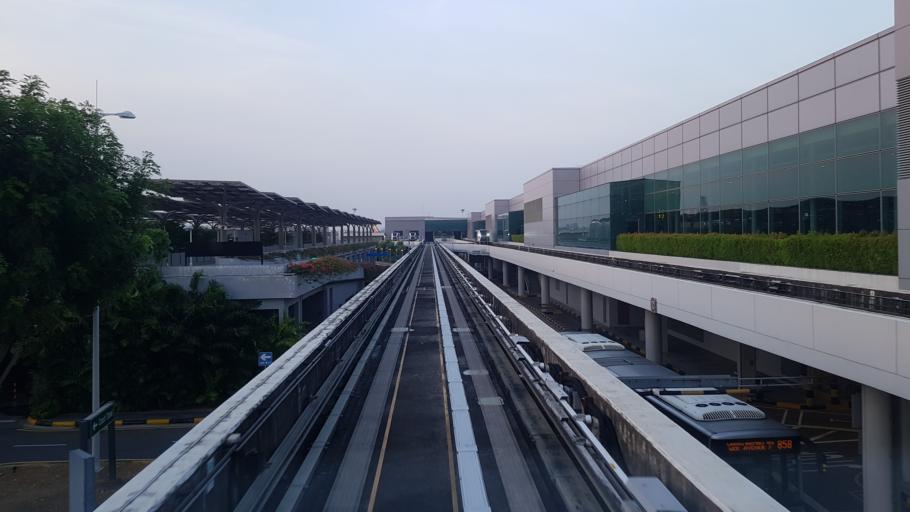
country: SG
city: Singapore
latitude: 1.3527
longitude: 103.9850
